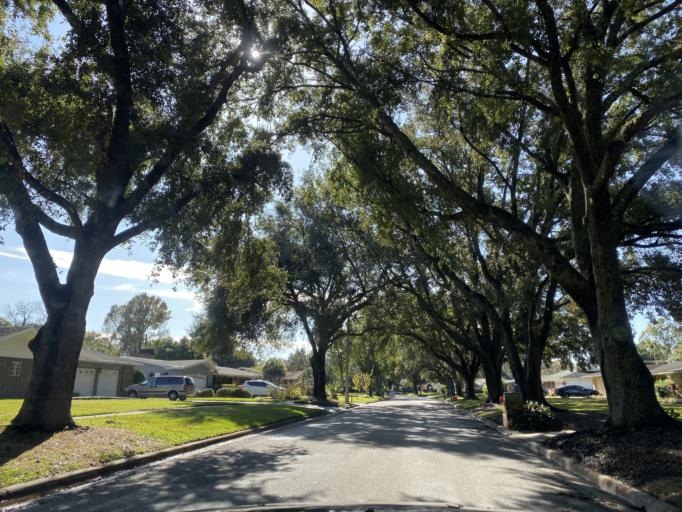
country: US
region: Florida
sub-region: Orange County
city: Azalea Park
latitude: 28.5297
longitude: -81.2634
